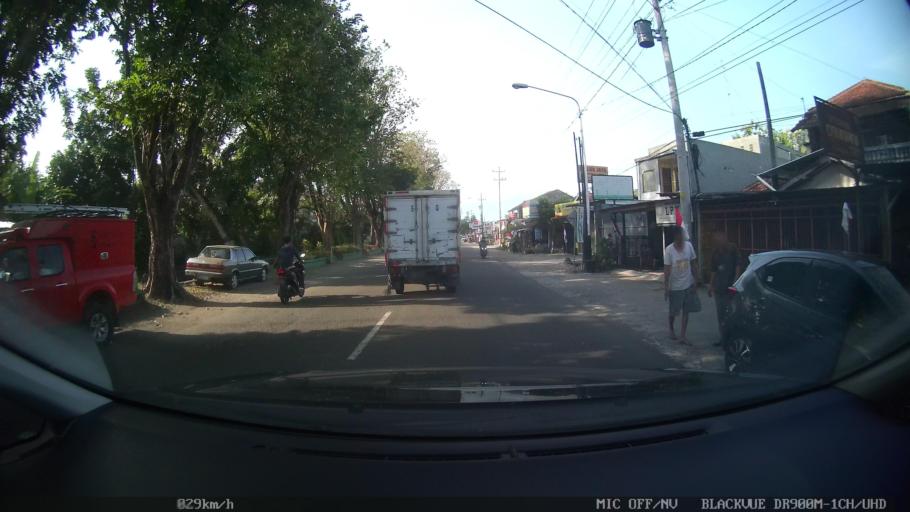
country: ID
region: Daerah Istimewa Yogyakarta
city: Bantul
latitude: -7.8997
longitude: 110.3221
